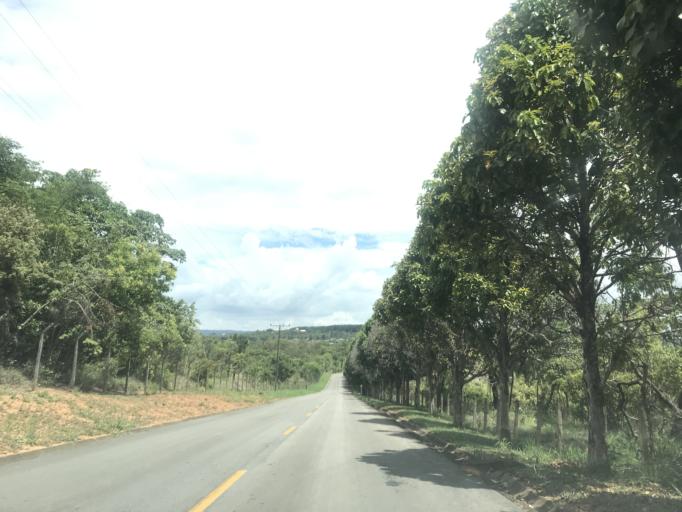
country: BR
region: Federal District
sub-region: Brasilia
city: Brasilia
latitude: -15.8006
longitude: -47.7996
